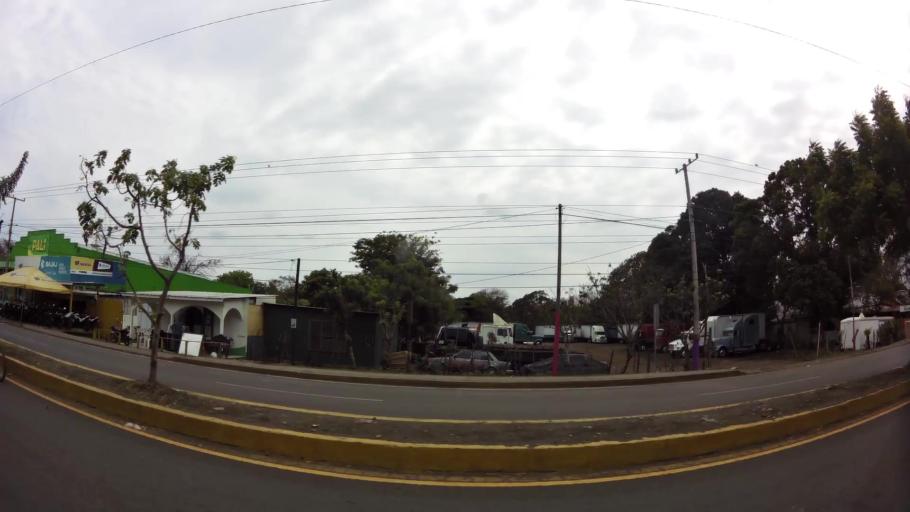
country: NI
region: Masaya
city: Masaya
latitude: 11.9773
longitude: -86.0796
